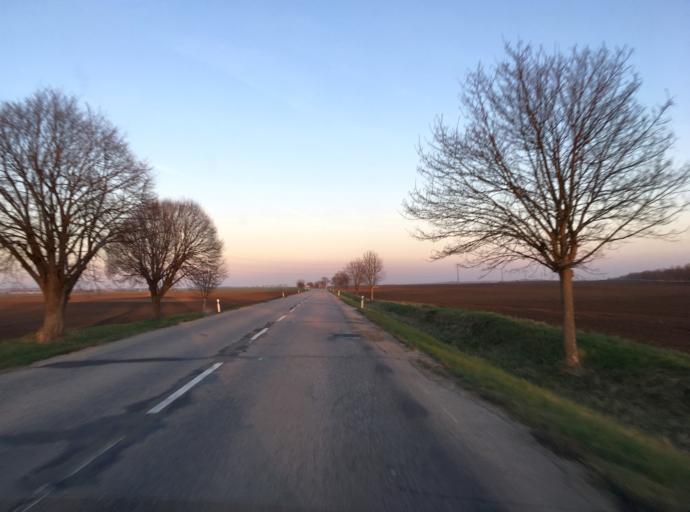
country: SK
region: Nitriansky
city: Svodin
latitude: 47.8989
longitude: 18.3666
